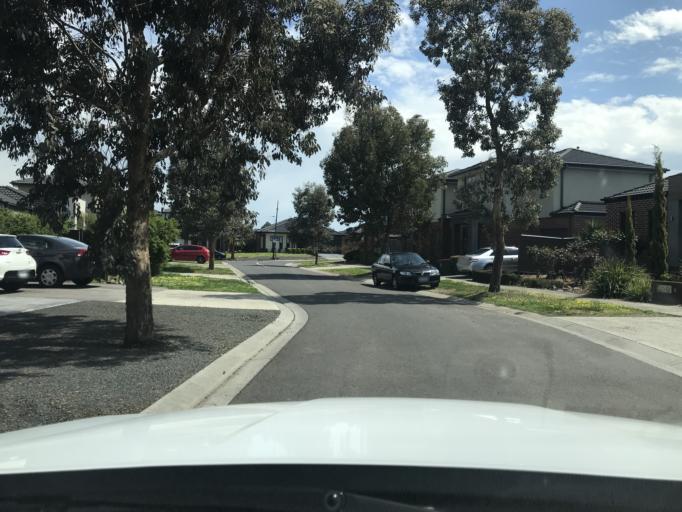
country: AU
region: Victoria
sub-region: Hume
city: Roxburgh Park
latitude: -37.5968
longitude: 144.9113
